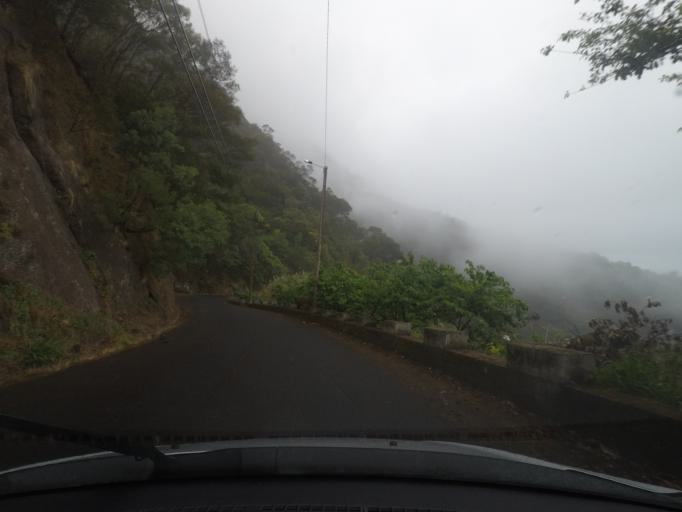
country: PT
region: Madeira
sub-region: Santana
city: Santana
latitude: 32.7804
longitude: -16.8619
